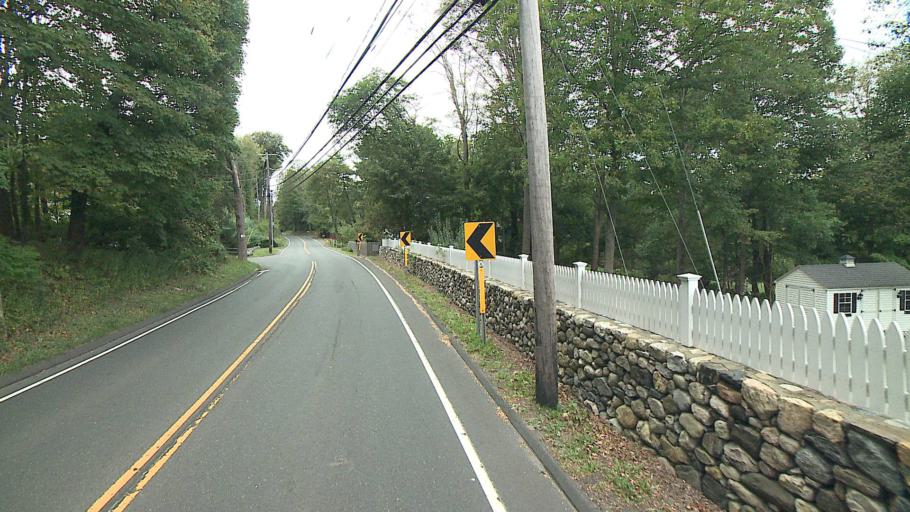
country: US
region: Connecticut
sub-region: Fairfield County
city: Wilton
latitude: 41.2087
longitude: -73.4560
